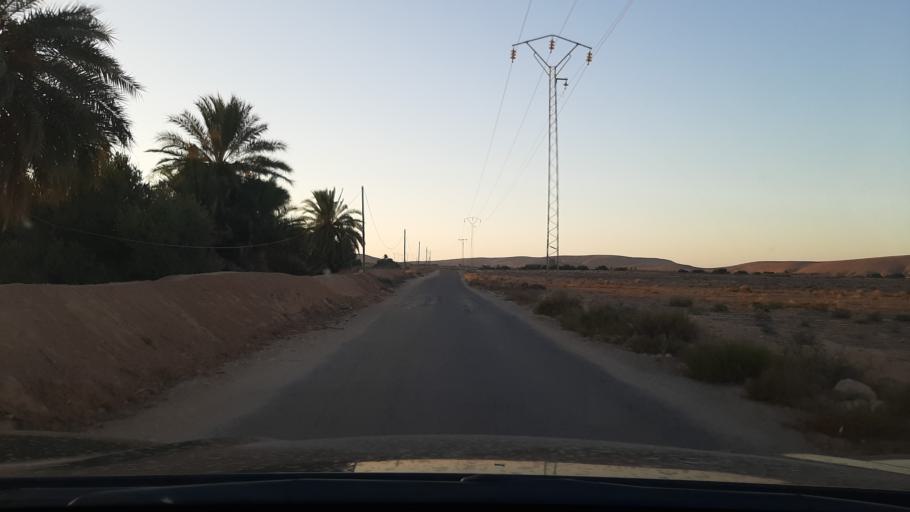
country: TN
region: Qabis
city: Matmata
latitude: 33.5455
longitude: 10.1921
